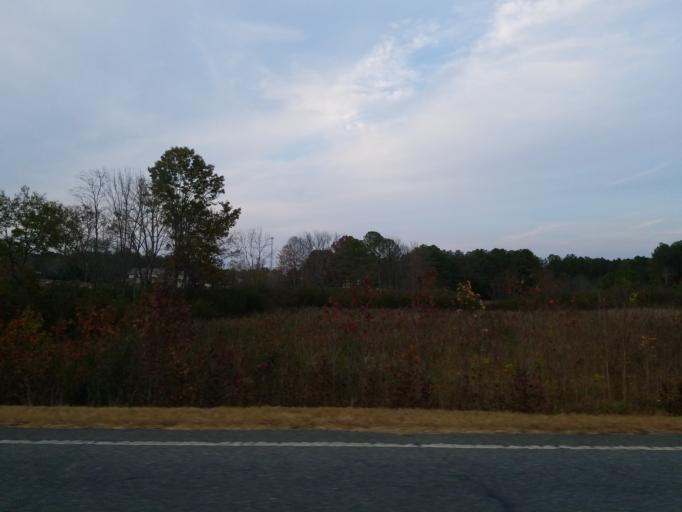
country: US
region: Georgia
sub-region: Gordon County
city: Calhoun
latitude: 34.6045
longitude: -84.8192
